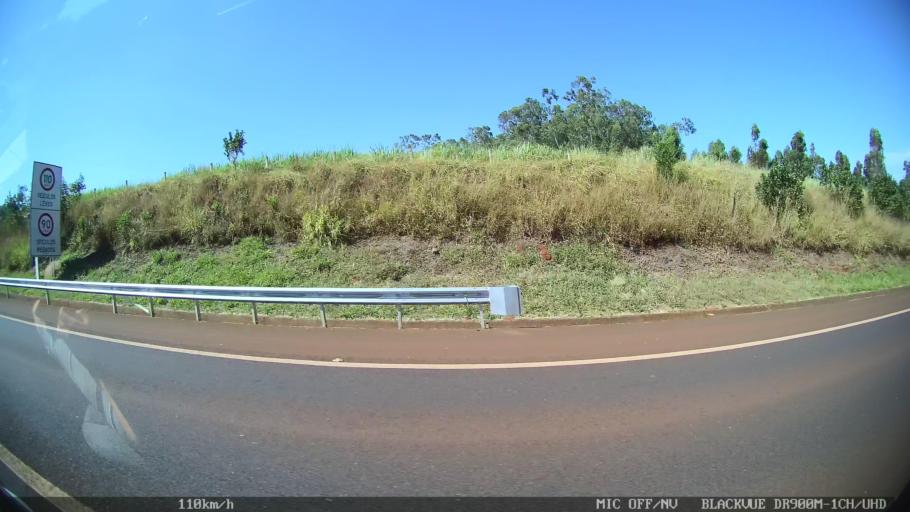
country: BR
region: Sao Paulo
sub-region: Franca
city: Franca
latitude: -20.6264
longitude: -47.4633
